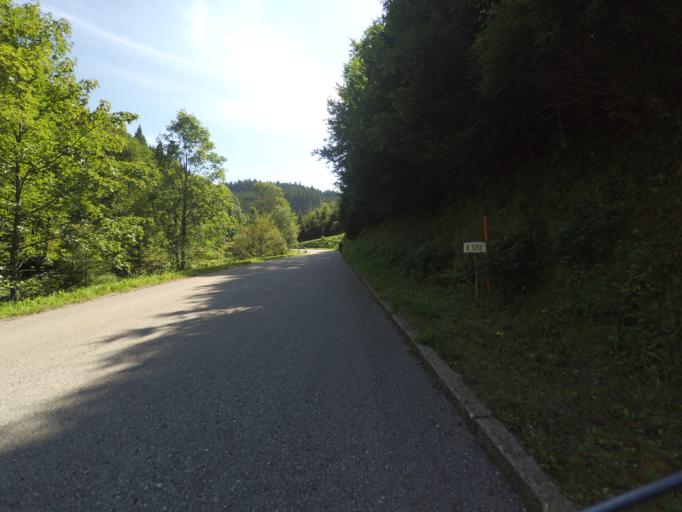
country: DE
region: Baden-Wuerttemberg
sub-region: Freiburg Region
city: Furtwangen im Schwarzwald
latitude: 48.0128
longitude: 8.1829
